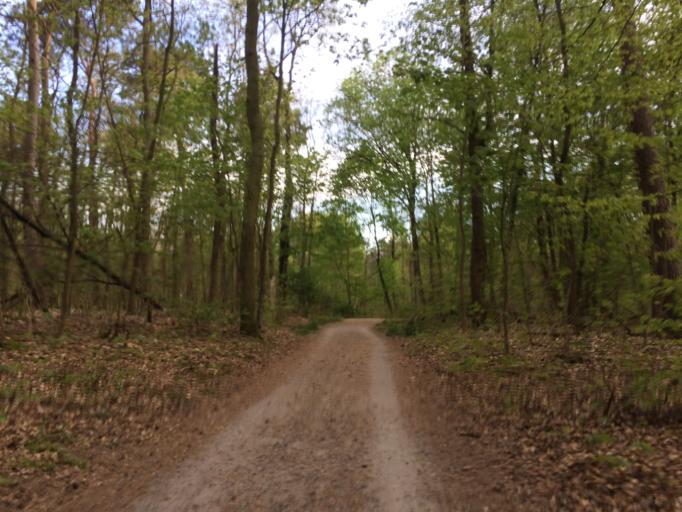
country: DE
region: Berlin
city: Buch
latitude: 52.6438
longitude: 13.4837
